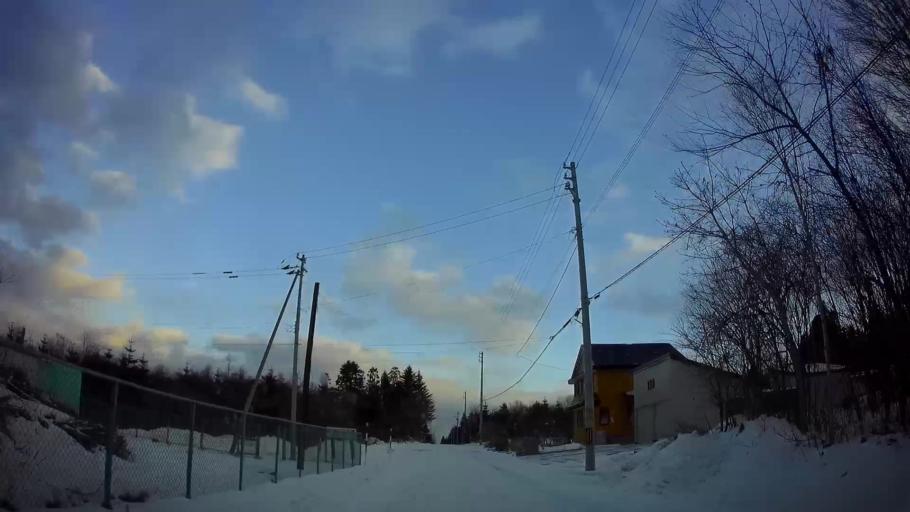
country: JP
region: Hokkaido
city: Nanae
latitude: 42.0222
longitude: 140.8347
